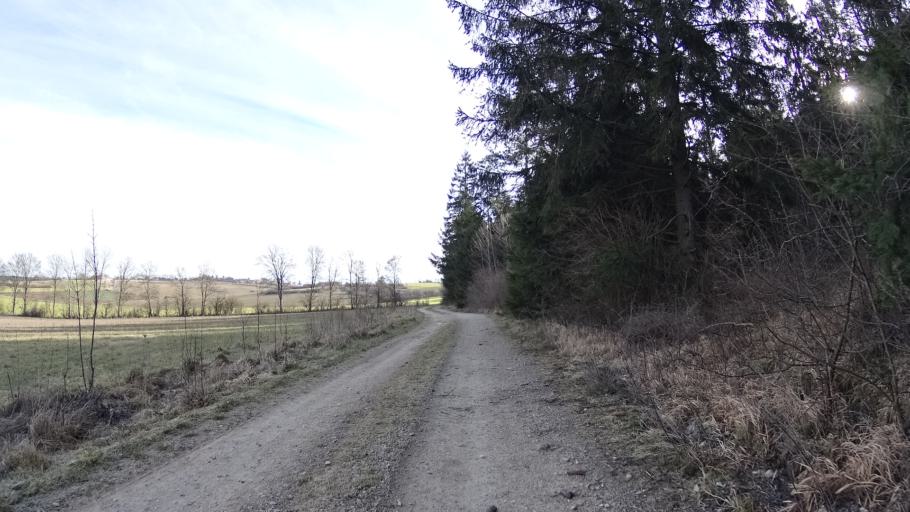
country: DE
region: Bavaria
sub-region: Upper Bavaria
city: Bohmfeld
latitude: 48.8567
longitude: 11.3457
